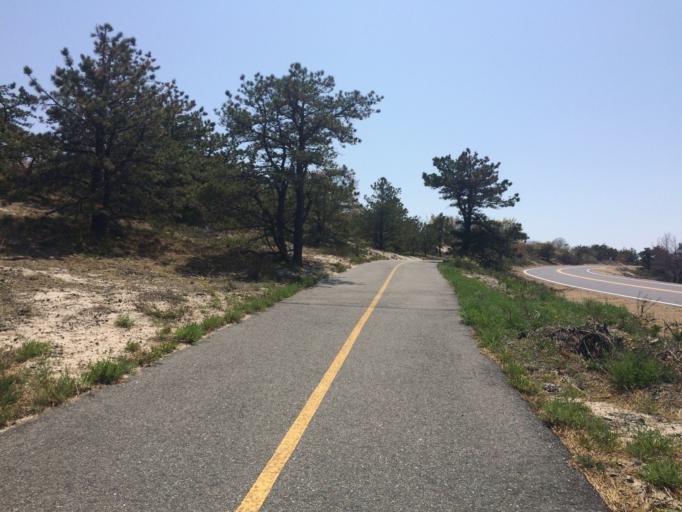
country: US
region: Massachusetts
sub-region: Barnstable County
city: Provincetown
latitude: 42.0692
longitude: -70.2104
